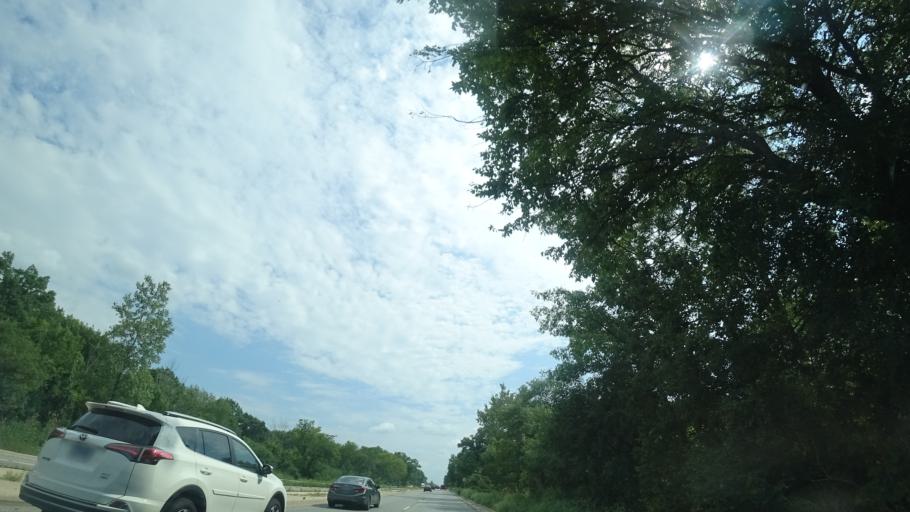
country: US
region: Illinois
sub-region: Cook County
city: Palos Heights
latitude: 41.6513
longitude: -87.7959
